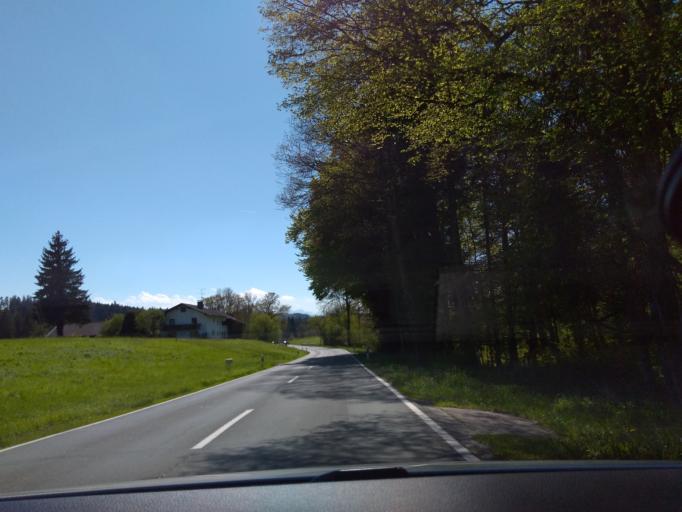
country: DE
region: Bavaria
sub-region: Upper Bavaria
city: Rimsting
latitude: 47.8611
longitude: 12.3014
